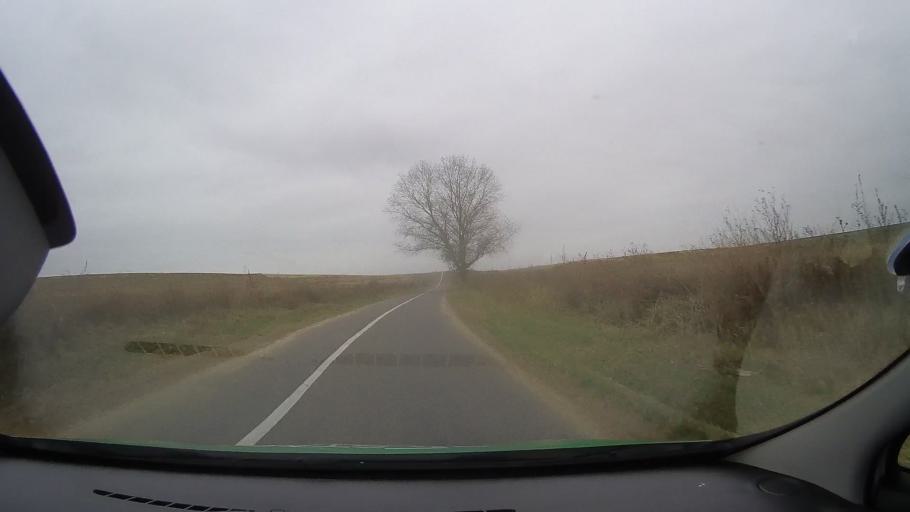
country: RO
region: Constanta
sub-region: Comuna Saraiu
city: Saraiu
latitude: 44.7247
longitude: 28.1855
